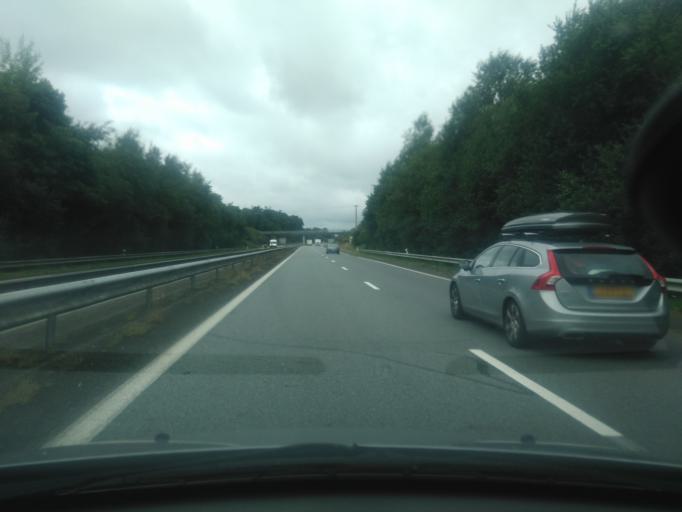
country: FR
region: Brittany
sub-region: Departement des Cotes-d'Armor
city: Trelivan
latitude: 48.4316
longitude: -2.1585
